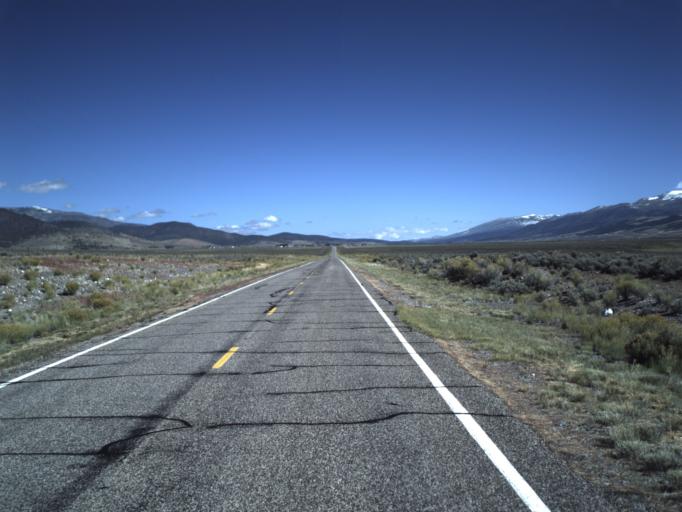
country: US
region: Utah
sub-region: Wayne County
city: Loa
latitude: 38.3879
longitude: -111.9336
